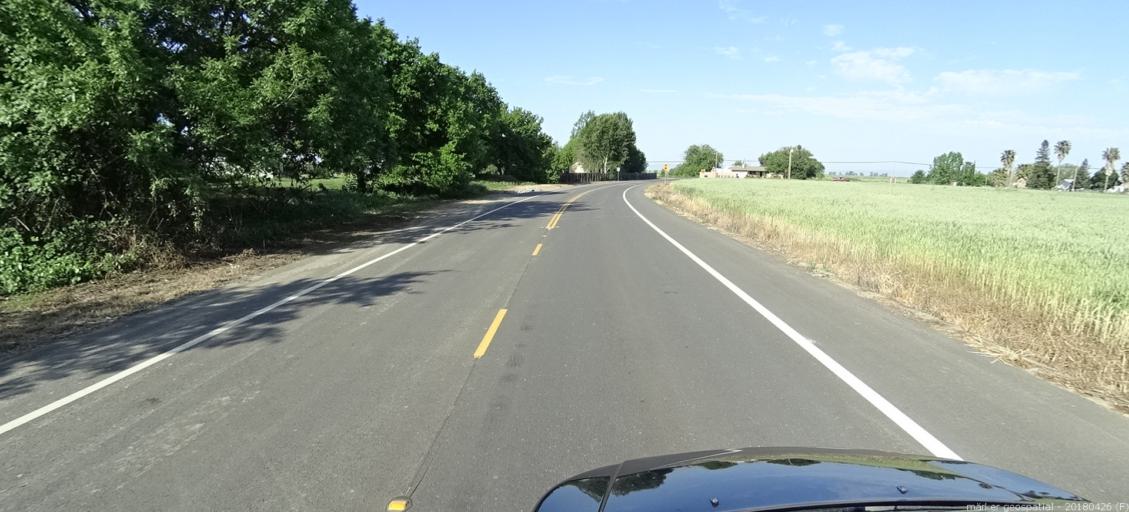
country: US
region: California
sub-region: Yolo County
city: West Sacramento
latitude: 38.5203
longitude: -121.5540
